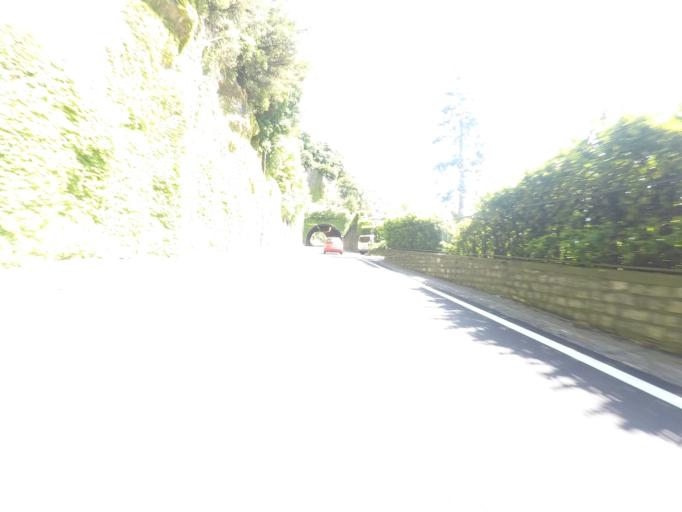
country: IT
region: Lombardy
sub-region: Provincia di Como
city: Moltrasio
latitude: 45.8542
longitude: 9.0903
